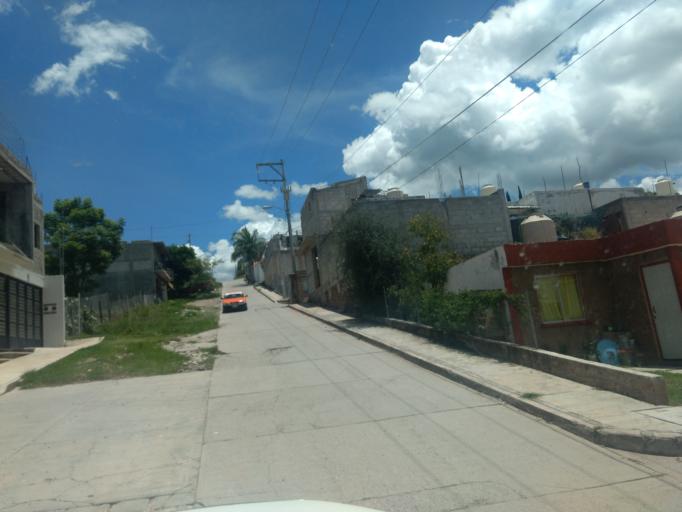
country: MX
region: Oaxaca
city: Ciudad de Huajuapam de Leon
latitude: 17.8158
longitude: -97.7951
